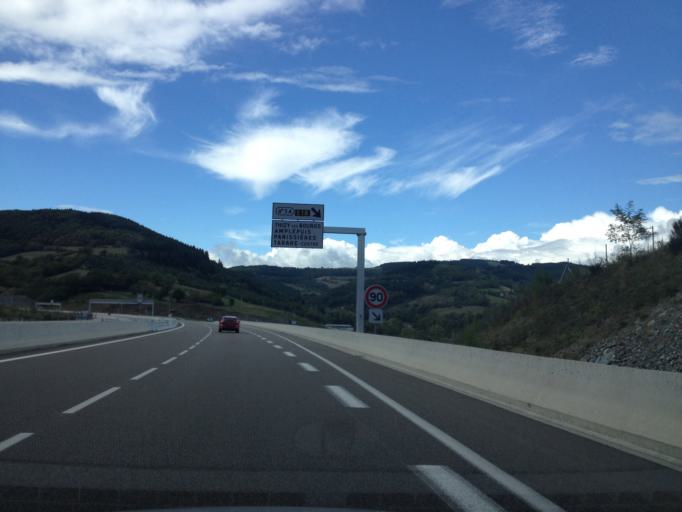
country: FR
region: Rhone-Alpes
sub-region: Departement du Rhone
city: Tarare
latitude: 45.8889
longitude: 4.4138
